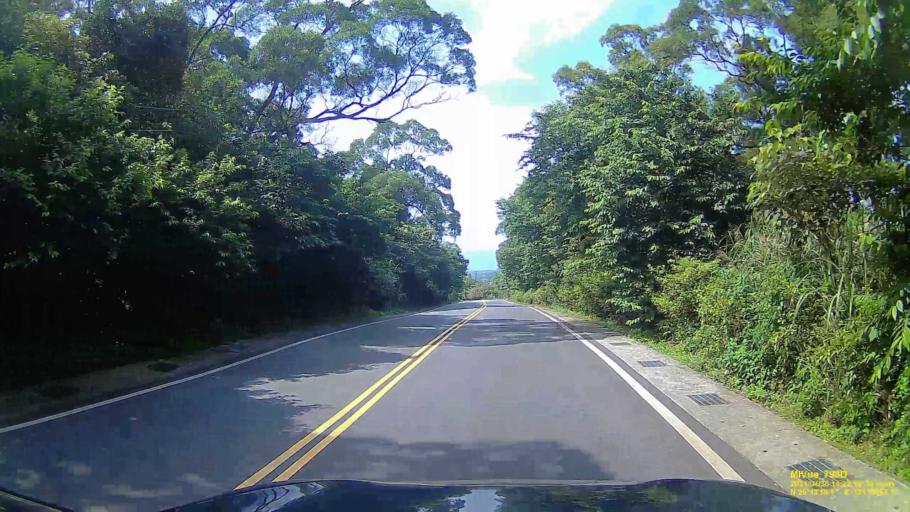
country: TW
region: Taipei
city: Taipei
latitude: 25.2223
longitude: 121.5142
